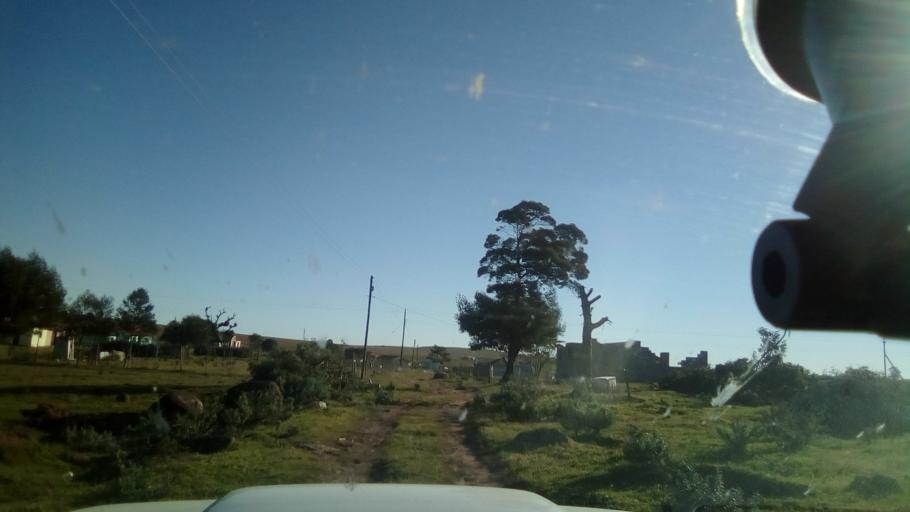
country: ZA
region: Eastern Cape
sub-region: Buffalo City Metropolitan Municipality
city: Bhisho
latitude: -32.9487
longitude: 27.2949
